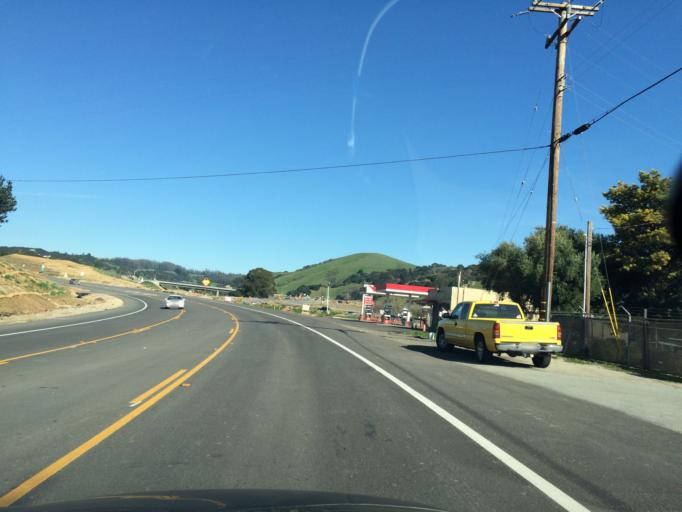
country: US
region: California
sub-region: San Benito County
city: Aromas
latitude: 36.8550
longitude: -121.6343
